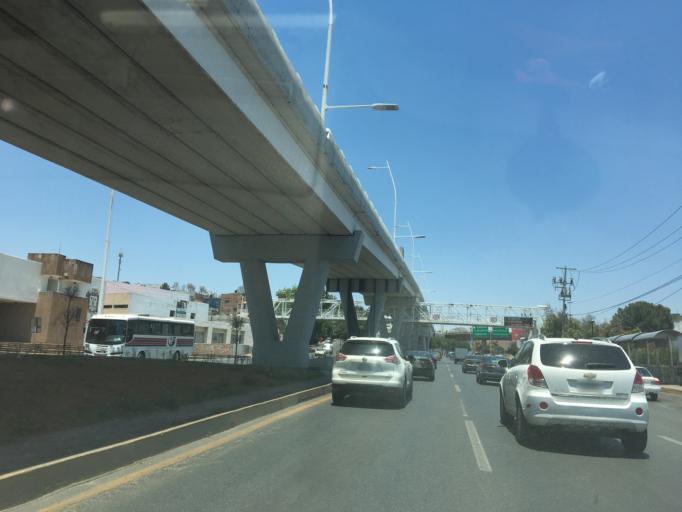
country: MX
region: Zacatecas
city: Zacatecas
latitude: 22.7736
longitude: -102.5878
